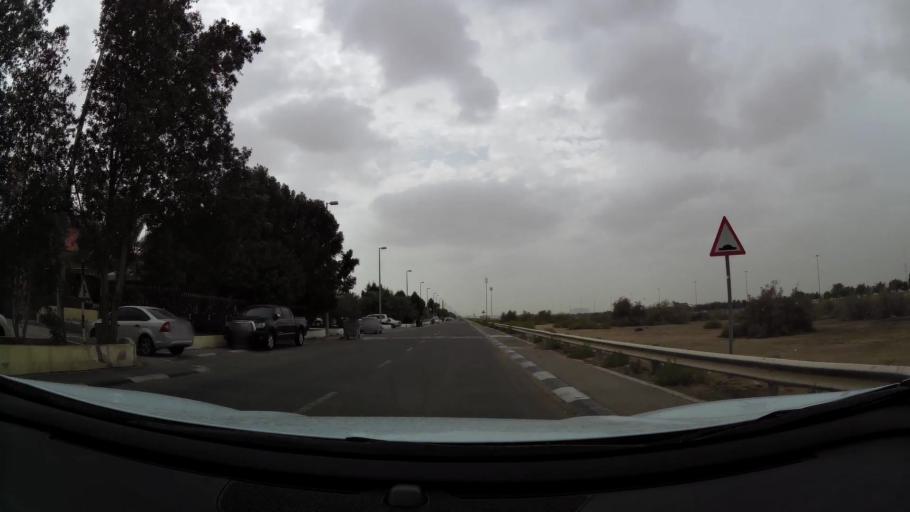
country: AE
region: Abu Dhabi
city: Abu Dhabi
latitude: 24.3597
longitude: 54.6521
